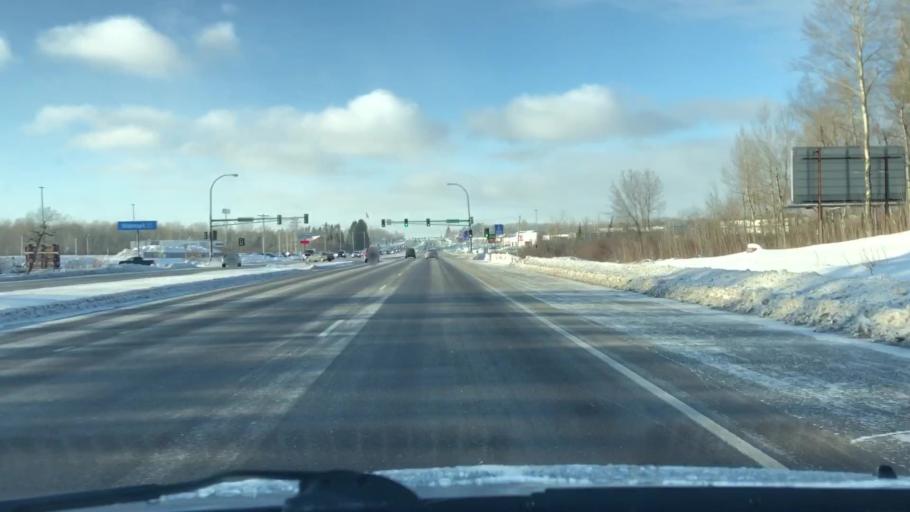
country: US
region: Minnesota
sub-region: Saint Louis County
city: Hermantown
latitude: 46.8184
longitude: -92.1805
